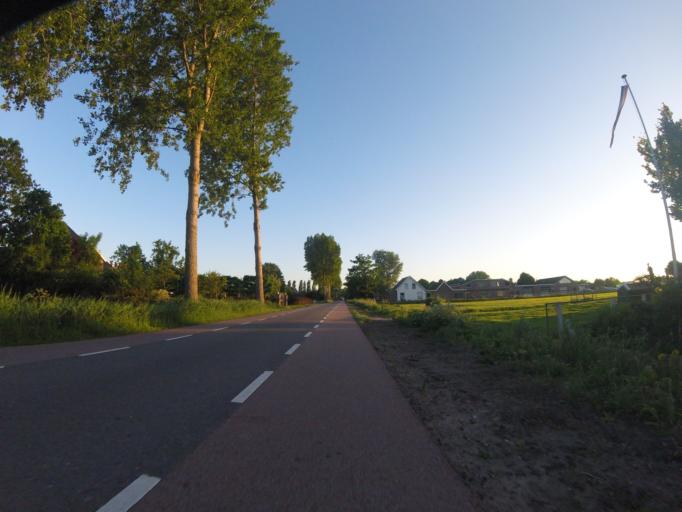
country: NL
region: North Holland
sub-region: Gemeente Haarlemmermeer
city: Hoofddorp
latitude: 52.3613
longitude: 4.6933
